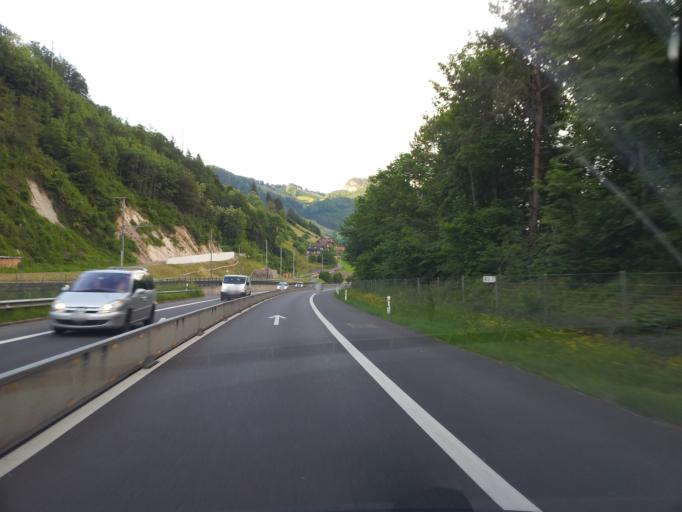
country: CH
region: Obwalden
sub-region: Obwalden
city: Alpnach
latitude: 46.9563
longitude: 8.2792
